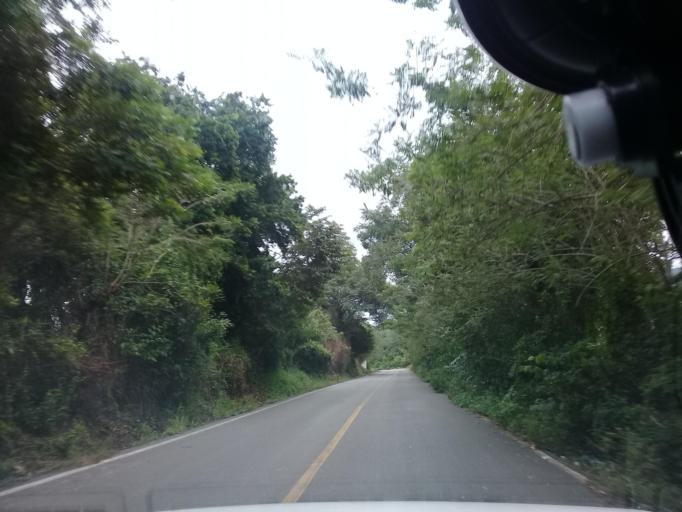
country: MX
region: Veracruz
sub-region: Chalma
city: San Pedro Coyutla
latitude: 21.2095
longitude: -98.4093
